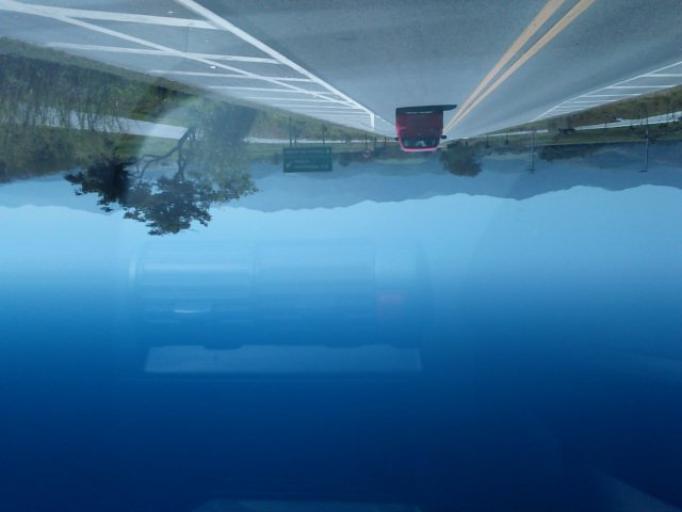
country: BR
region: Sao Paulo
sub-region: Taubate
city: Taubate
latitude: -22.9970
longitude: -45.6421
